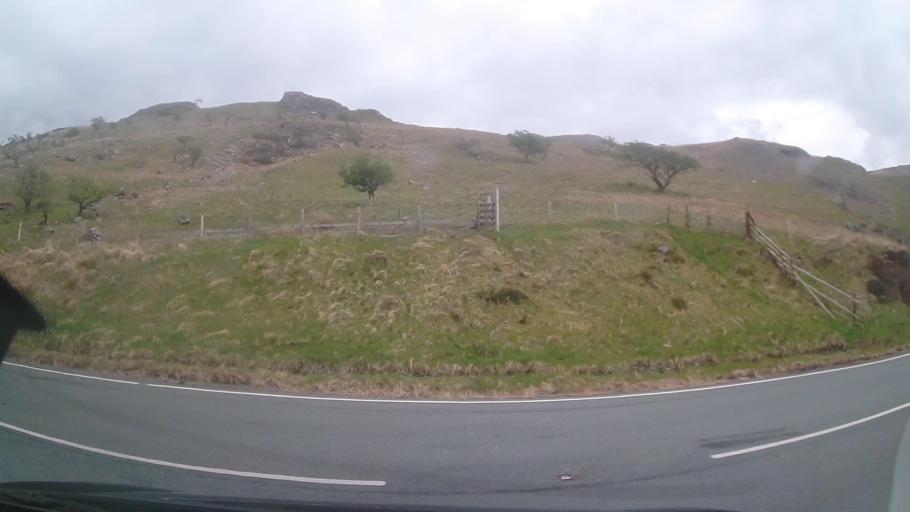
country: GB
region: Wales
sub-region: Gwynedd
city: Blaenau-Ffestiniog
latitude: 53.0676
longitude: -4.0041
